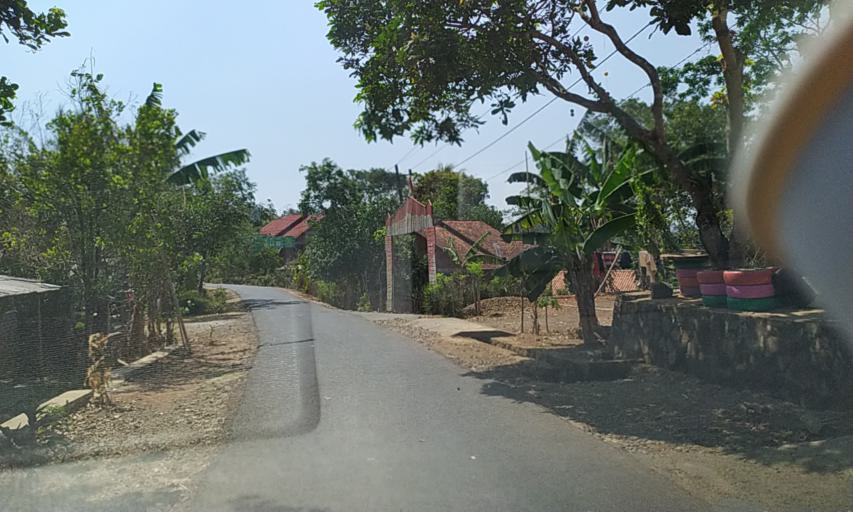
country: ID
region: Central Java
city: Rungkang
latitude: -7.4357
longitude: 108.8517
